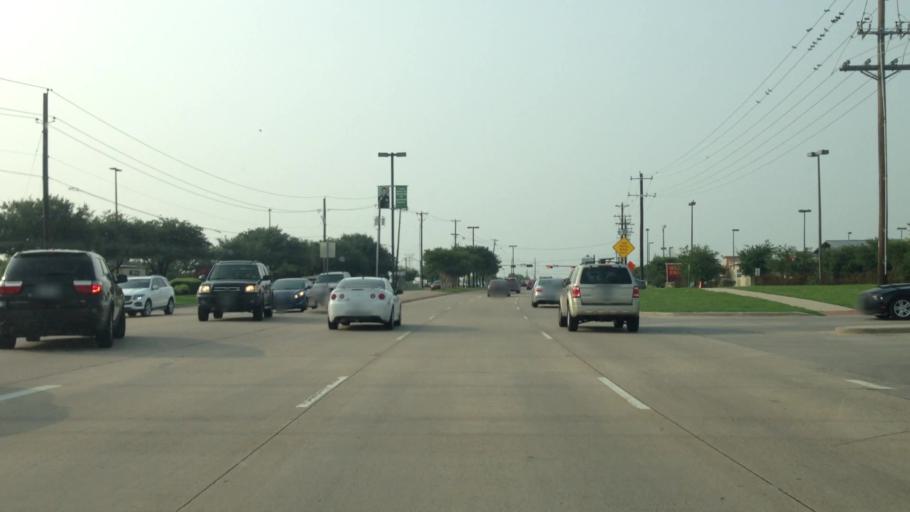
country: US
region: Texas
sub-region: Dallas County
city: Carrollton
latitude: 33.0184
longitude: -96.9150
